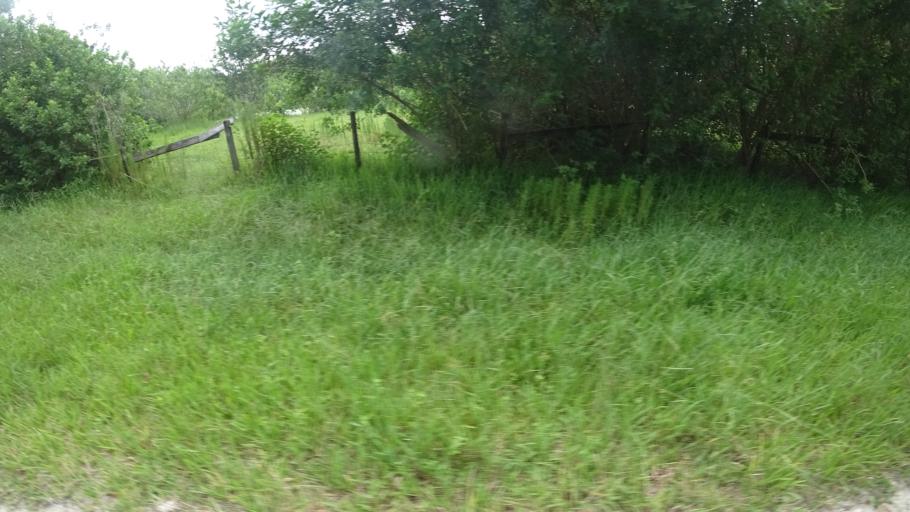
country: US
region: Florida
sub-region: Sarasota County
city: The Meadows
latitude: 27.4508
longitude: -82.2787
